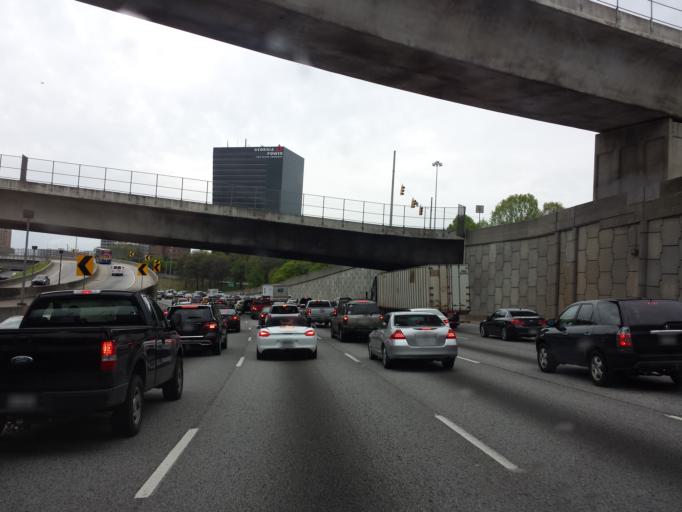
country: US
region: Georgia
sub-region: Fulton County
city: Atlanta
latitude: 33.7595
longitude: -84.3789
